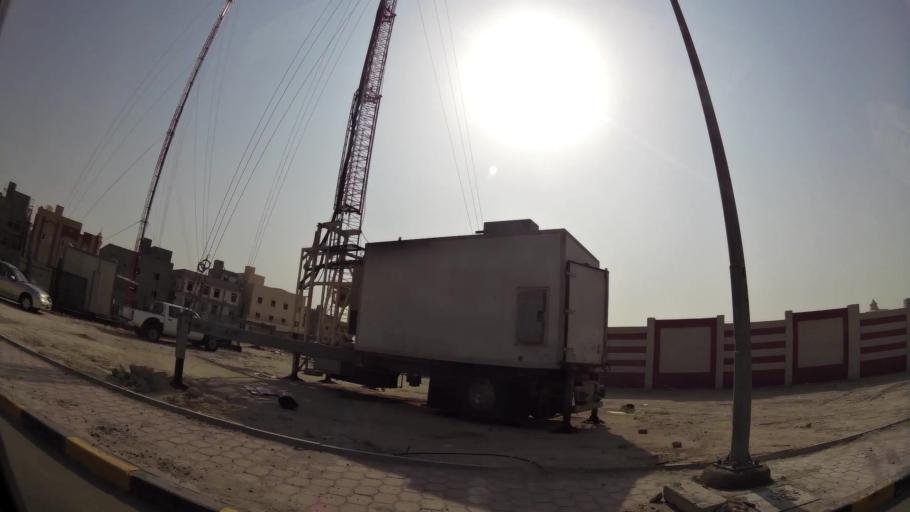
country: KW
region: Muhafazat al Jahra'
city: Al Jahra'
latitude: 29.3563
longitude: 47.7629
